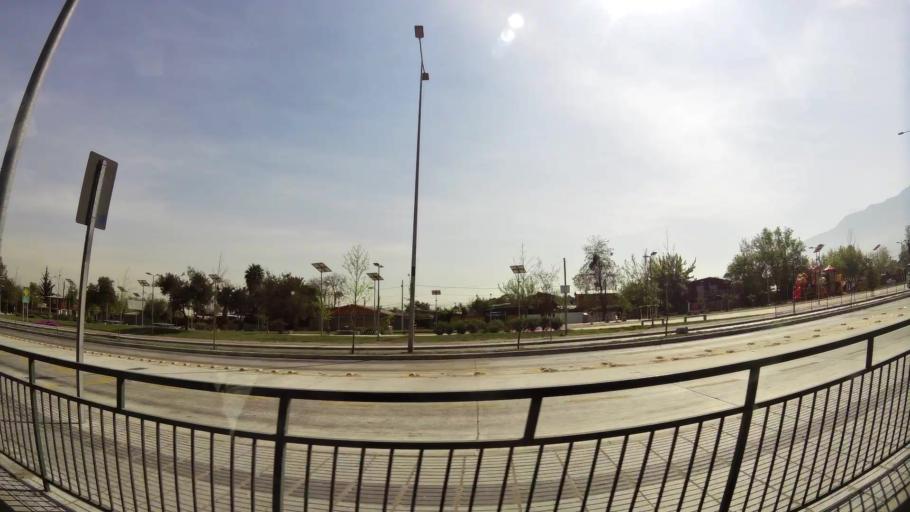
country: CL
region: Santiago Metropolitan
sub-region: Provincia de Santiago
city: Villa Presidente Frei, Nunoa, Santiago, Chile
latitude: -33.5114
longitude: -70.5633
